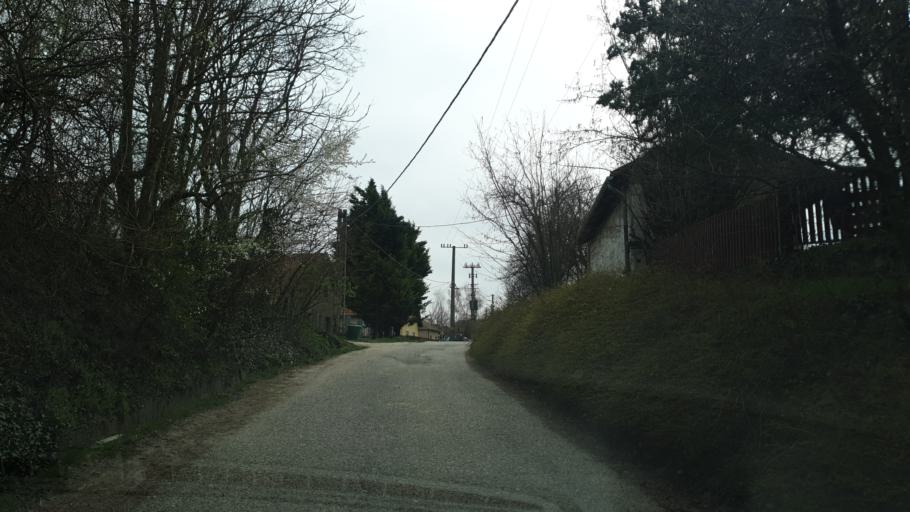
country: HU
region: Fejer
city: Etyek
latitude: 47.4425
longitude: 18.7485
